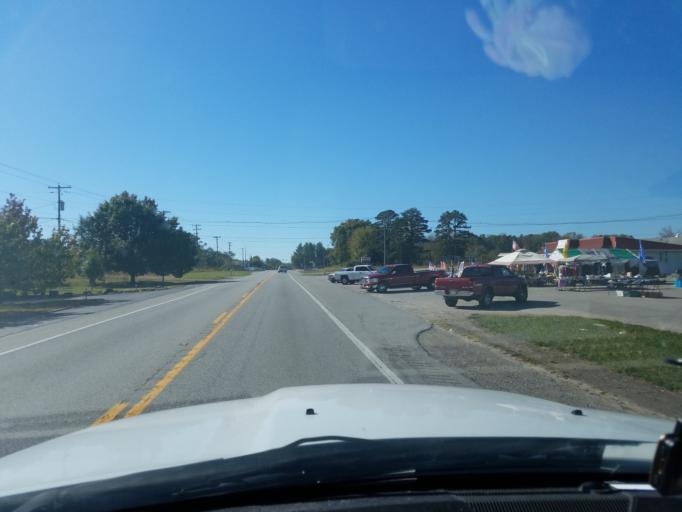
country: US
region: Kentucky
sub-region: Laurel County
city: North Corbin
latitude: 37.0332
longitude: -84.0611
